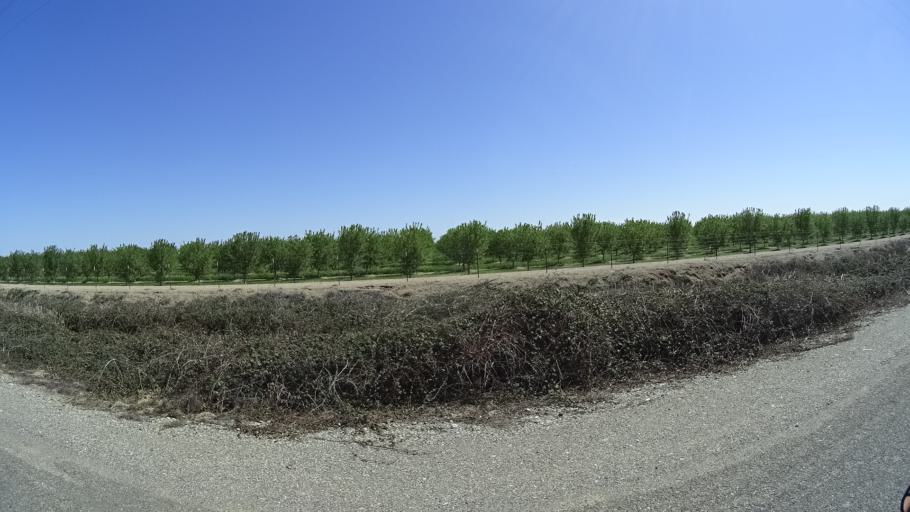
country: US
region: California
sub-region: Glenn County
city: Orland
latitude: 39.6728
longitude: -122.2343
